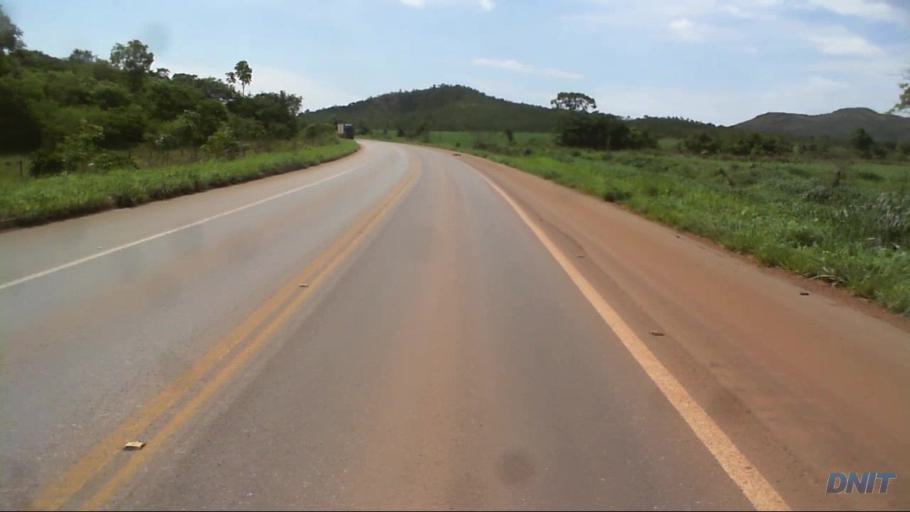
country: BR
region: Goias
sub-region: Barro Alto
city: Barro Alto
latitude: -15.1304
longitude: -48.8344
